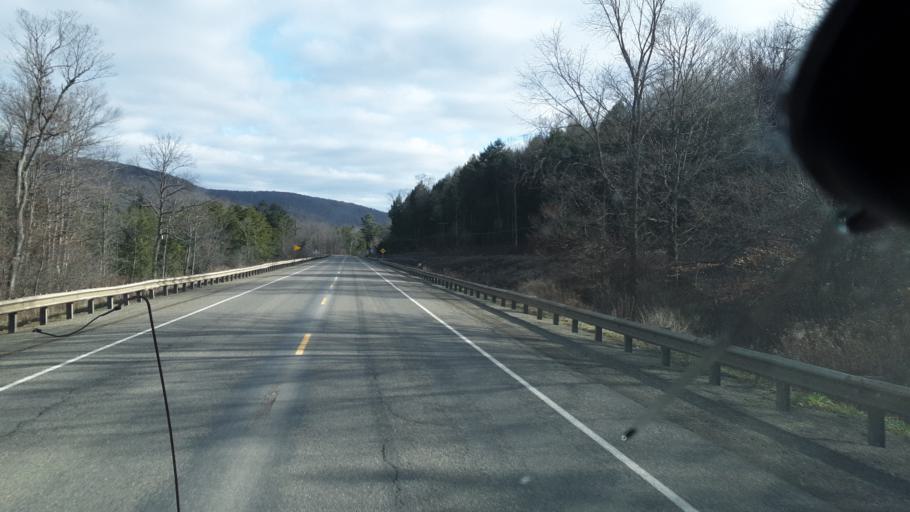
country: US
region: Pennsylvania
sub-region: Potter County
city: Galeton
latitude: 41.7895
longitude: -77.7696
